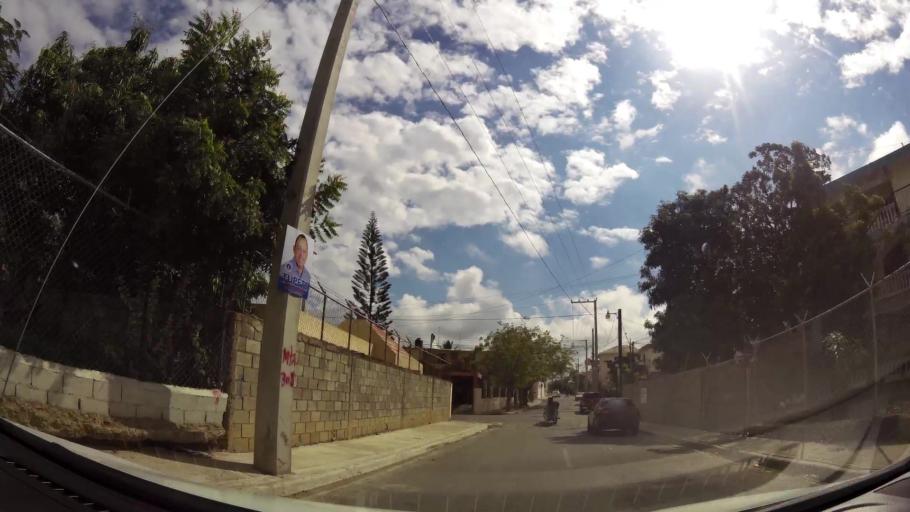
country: DO
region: Santiago
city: Santiago de los Caballeros
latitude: 19.4879
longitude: -70.7298
